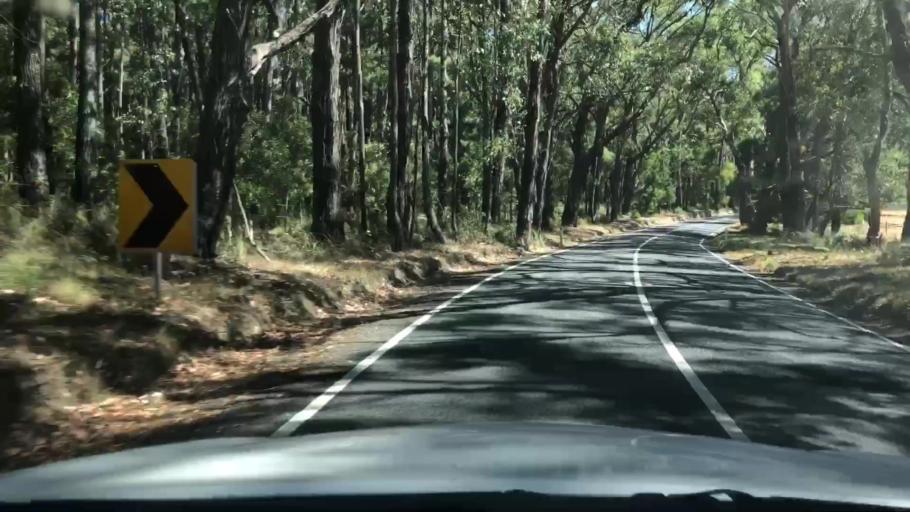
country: AU
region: Victoria
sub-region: Yarra Ranges
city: Macclesfield
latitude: -37.8504
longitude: 145.4876
